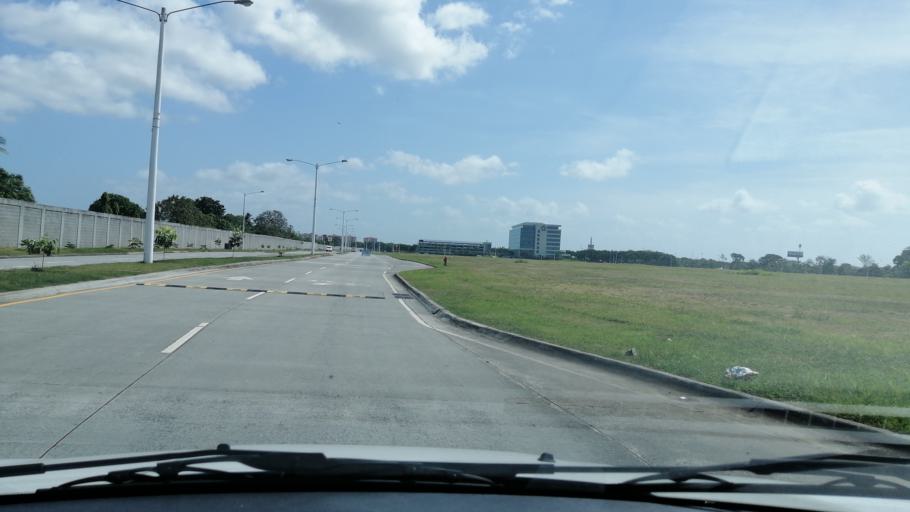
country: PA
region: Panama
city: San Miguelito
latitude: 9.0390
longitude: -79.4303
